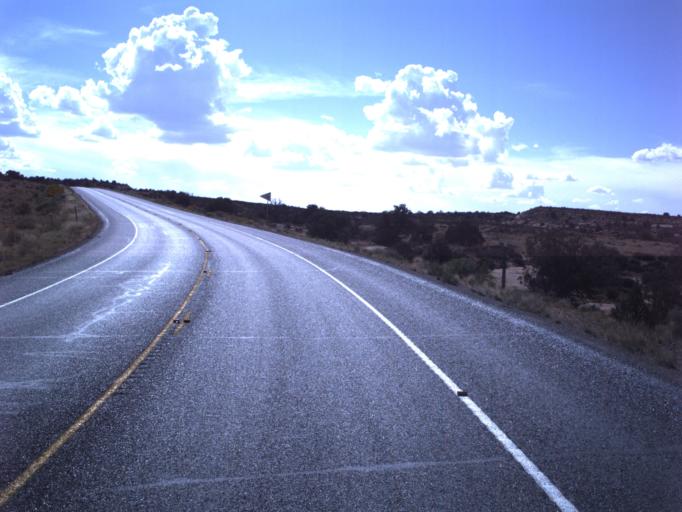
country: US
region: Utah
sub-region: Grand County
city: Moab
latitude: 38.6371
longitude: -109.7894
